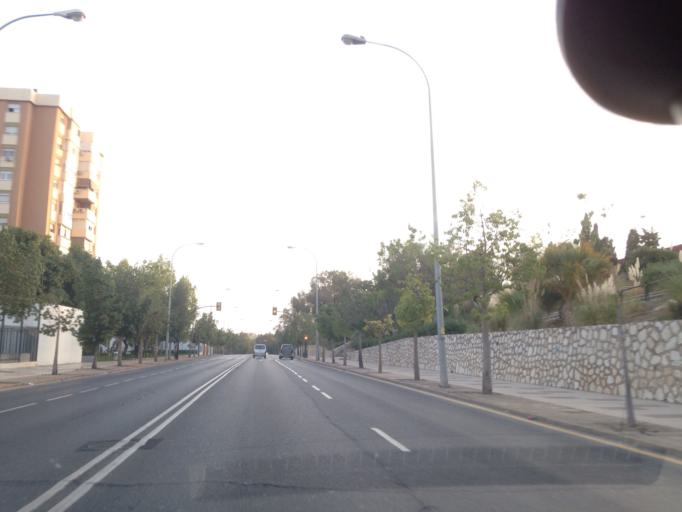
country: ES
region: Andalusia
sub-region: Provincia de Malaga
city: Malaga
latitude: 36.7331
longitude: -4.4336
